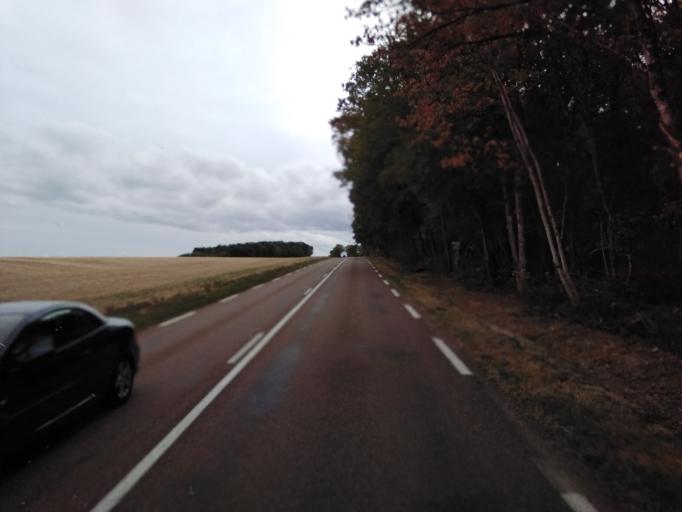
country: FR
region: Champagne-Ardenne
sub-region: Departement de l'Aube
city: Bar-sur-Seine
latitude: 48.1558
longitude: 4.4111
